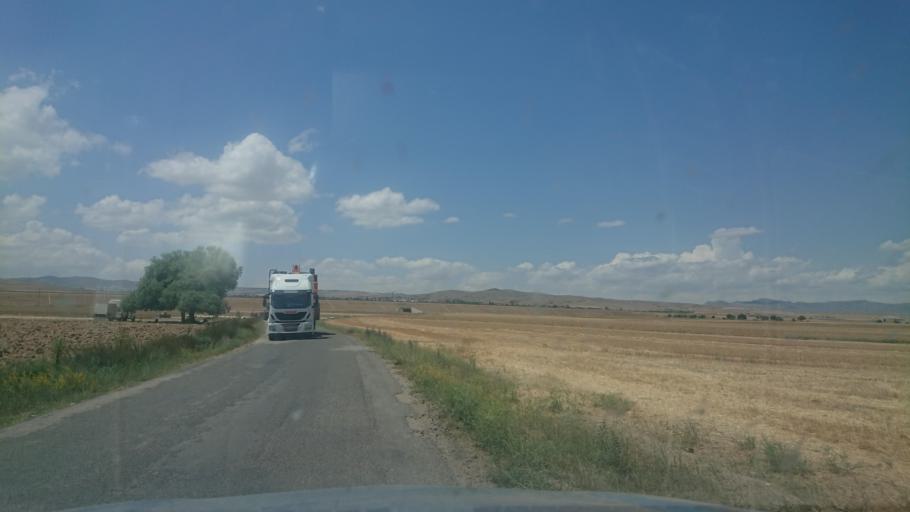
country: TR
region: Aksaray
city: Sariyahsi
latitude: 38.9947
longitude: 33.8749
